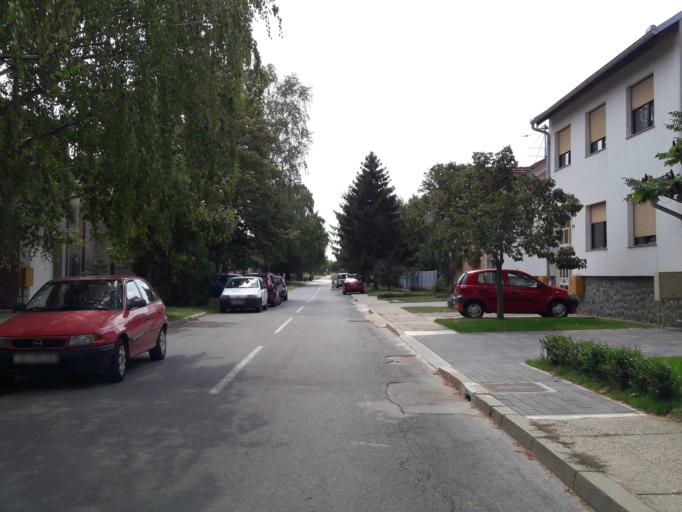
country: HR
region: Osjecko-Baranjska
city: Visnjevac
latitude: 45.5598
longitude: 18.6441
